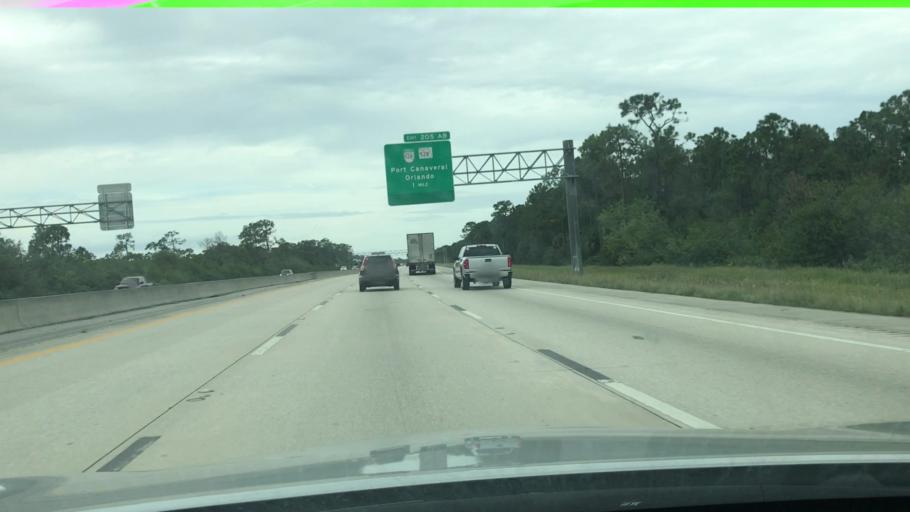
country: US
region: Florida
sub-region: Brevard County
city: Cocoa West
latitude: 28.3900
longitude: -80.8142
